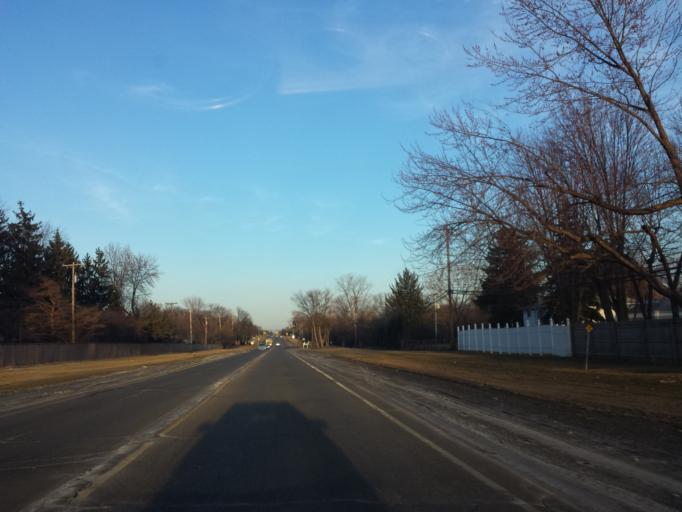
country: US
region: Michigan
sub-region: Oakland County
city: Beverly Hills
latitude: 42.5167
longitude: -83.2374
